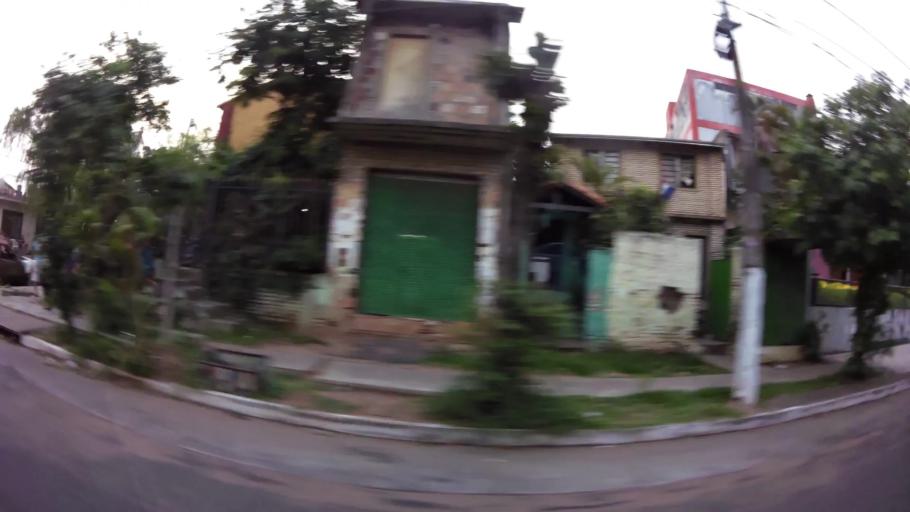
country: PY
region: Central
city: Lambare
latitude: -25.3203
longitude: -57.6148
